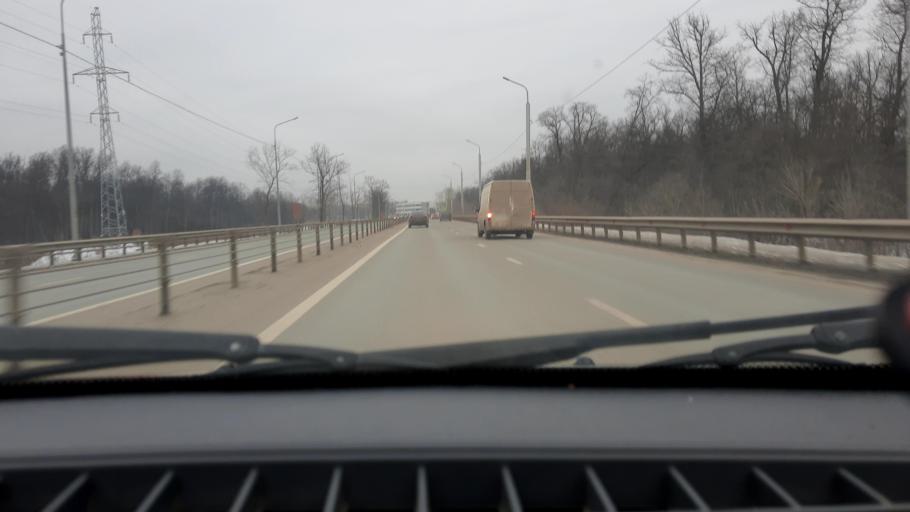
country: RU
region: Bashkortostan
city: Ufa
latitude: 54.6984
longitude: 55.8845
